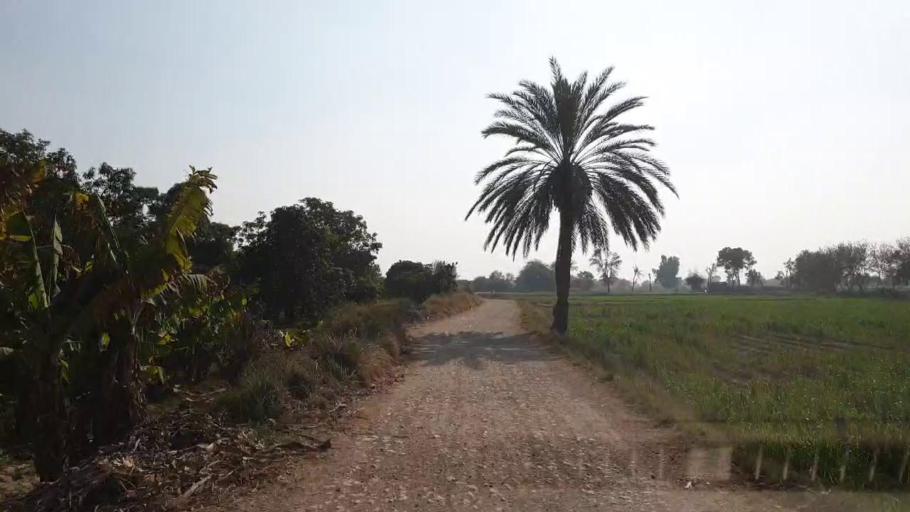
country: PK
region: Sindh
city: Tando Adam
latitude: 25.6801
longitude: 68.5663
